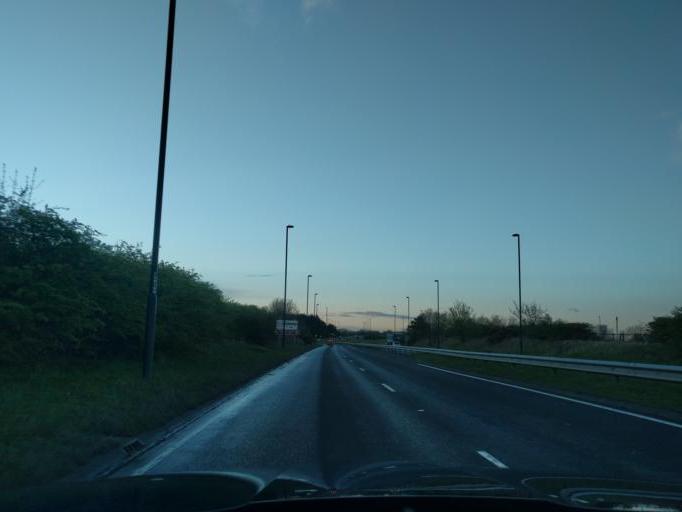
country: GB
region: England
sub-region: Newcastle upon Tyne
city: Gosforth
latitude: 55.0375
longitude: -1.5923
